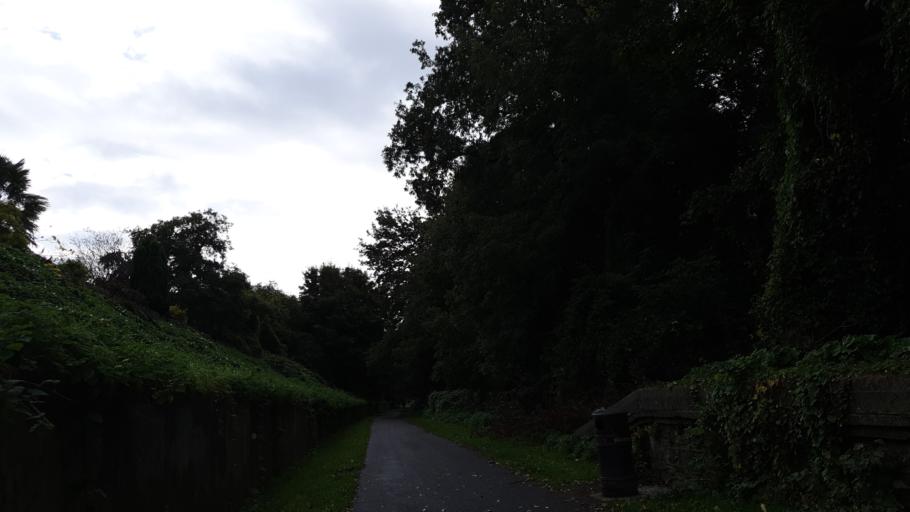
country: IE
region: Munster
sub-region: County Cork
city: Cork
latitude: 51.8955
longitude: -8.4177
